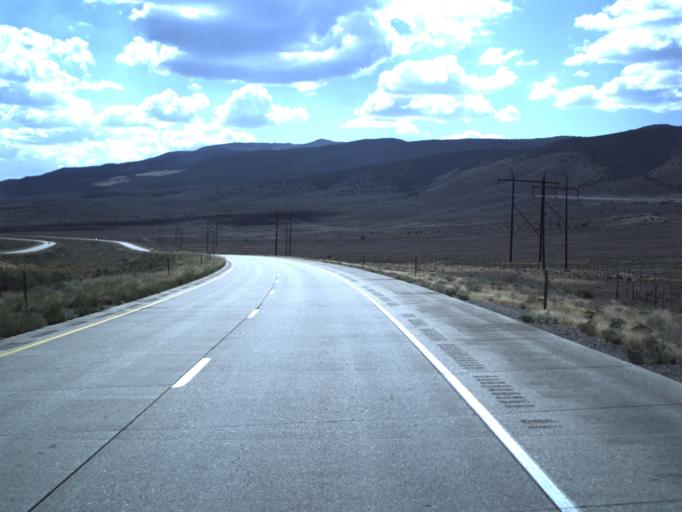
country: US
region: Utah
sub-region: Sevier County
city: Monroe
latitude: 38.6587
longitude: -112.1989
